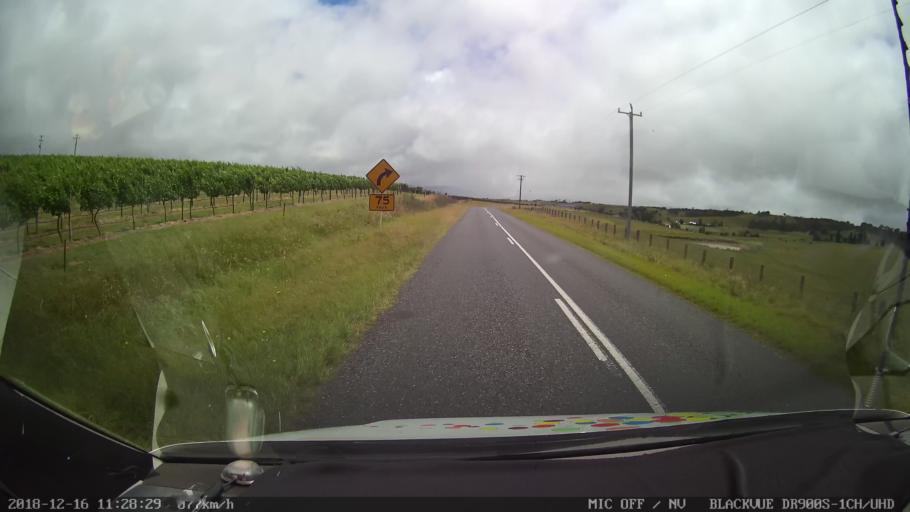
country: AU
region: New South Wales
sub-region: Tenterfield Municipality
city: Carrolls Creek
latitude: -29.0384
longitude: 152.0983
